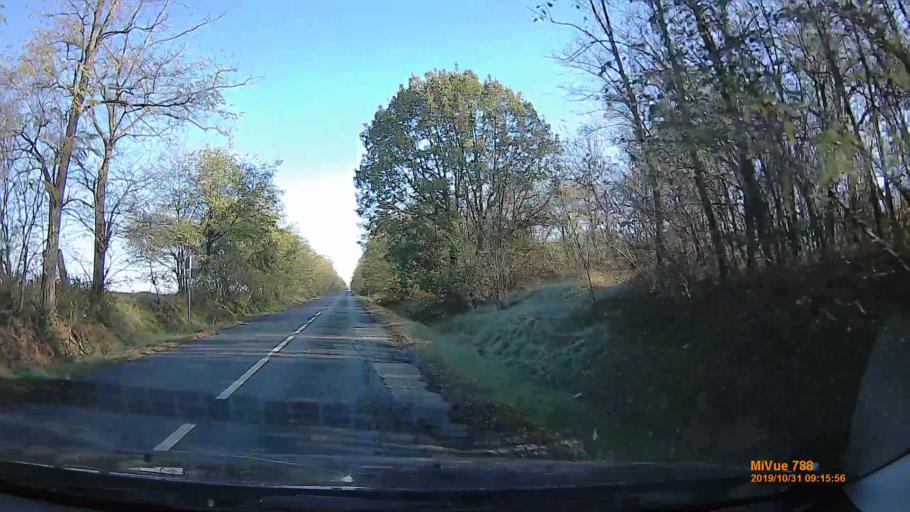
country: HU
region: Pest
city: Peteri
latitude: 47.3968
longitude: 19.4069
